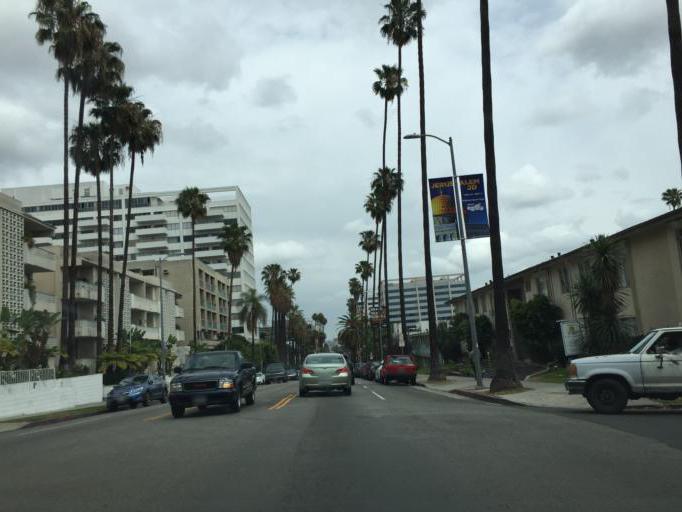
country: US
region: California
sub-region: Los Angeles County
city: West Hollywood
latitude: 34.1016
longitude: -118.3481
